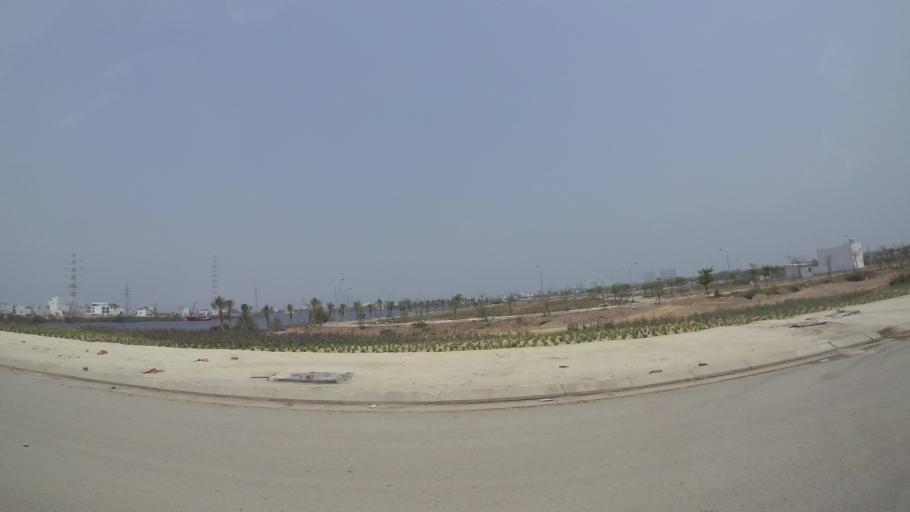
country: VN
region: Da Nang
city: Ngu Hanh Son
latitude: 16.0140
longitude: 108.2367
